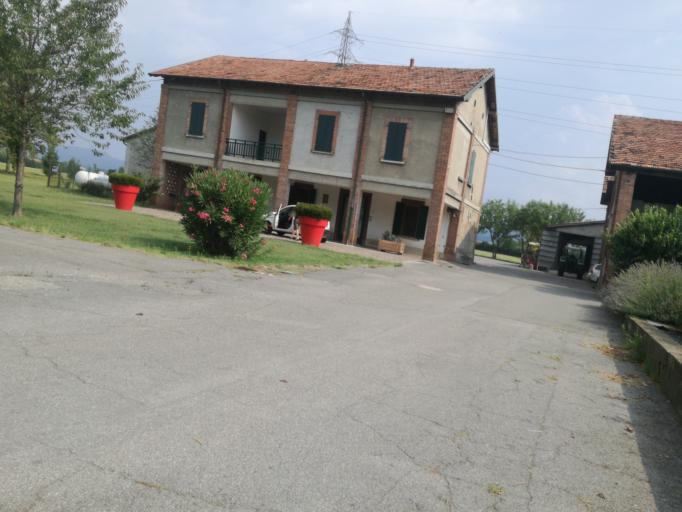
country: IT
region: Lombardy
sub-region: Provincia di Lecco
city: Verderio Superiore
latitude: 45.6650
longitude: 9.4559
